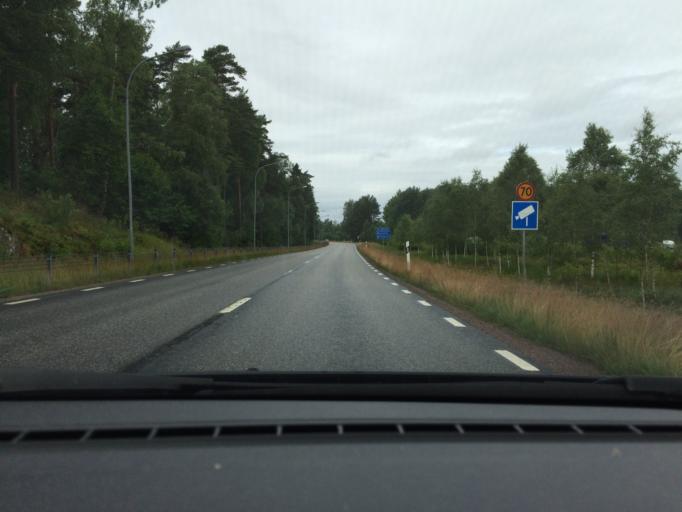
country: SE
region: Joenkoeping
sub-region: Varnamo Kommun
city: Forsheda
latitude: 57.1645
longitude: 13.8414
